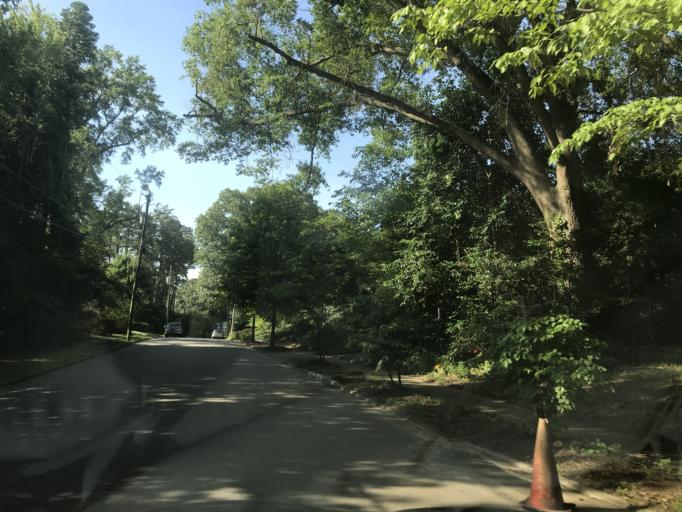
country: US
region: North Carolina
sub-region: Wake County
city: West Raleigh
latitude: 35.7947
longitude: -78.6775
